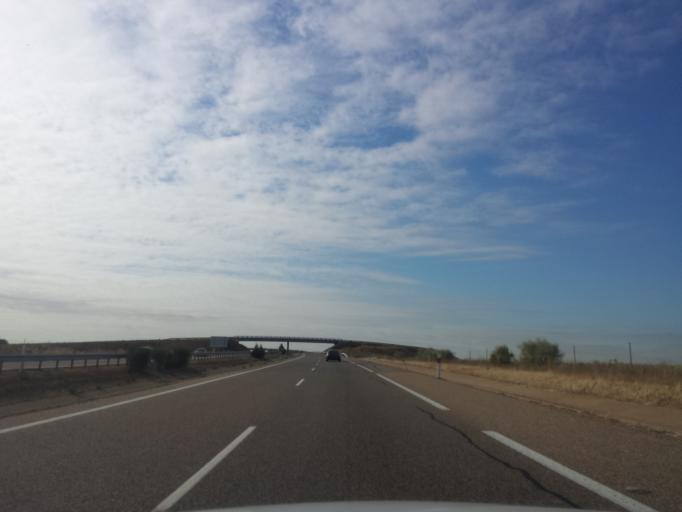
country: ES
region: Castille and Leon
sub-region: Provincia de Leon
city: Onzonilla
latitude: 42.4837
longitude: -5.5977
